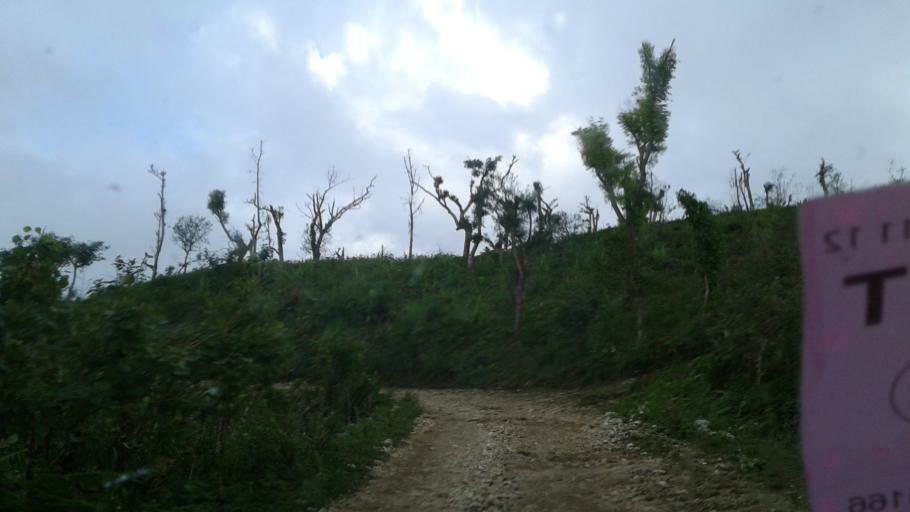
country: HT
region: Grandans
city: Jeremie
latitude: 18.4931
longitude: -74.1082
